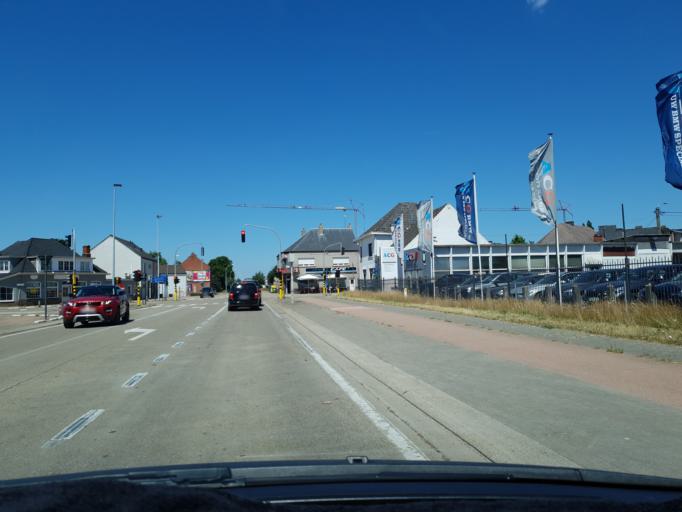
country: BE
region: Flanders
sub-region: Provincie Antwerpen
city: Westerlo
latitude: 51.0966
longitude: 4.9447
